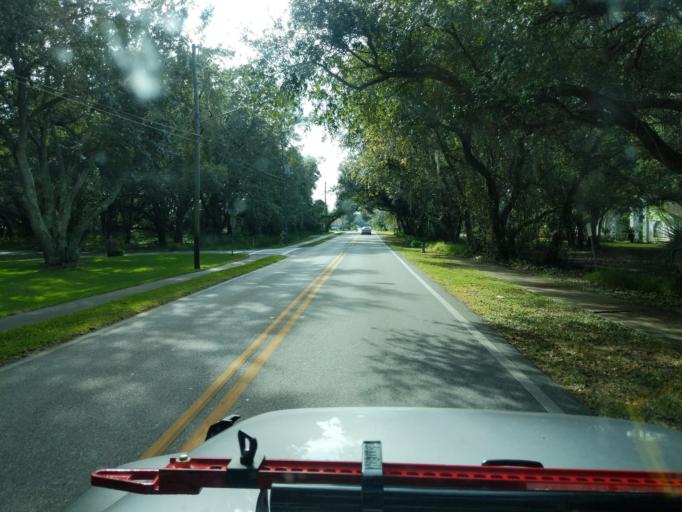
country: US
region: Florida
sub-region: Orange County
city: Gotha
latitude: 28.5204
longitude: -81.5361
